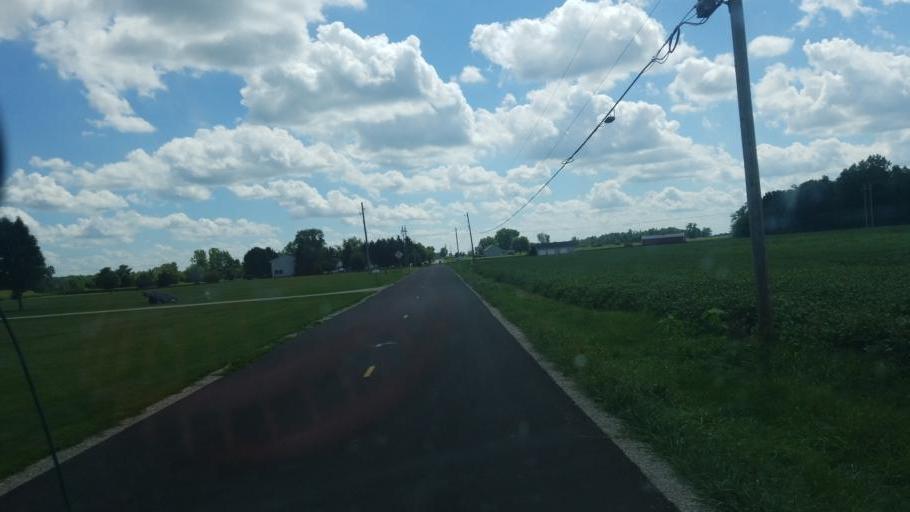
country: US
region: Ohio
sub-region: Marion County
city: Prospect
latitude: 40.5153
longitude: -83.1657
